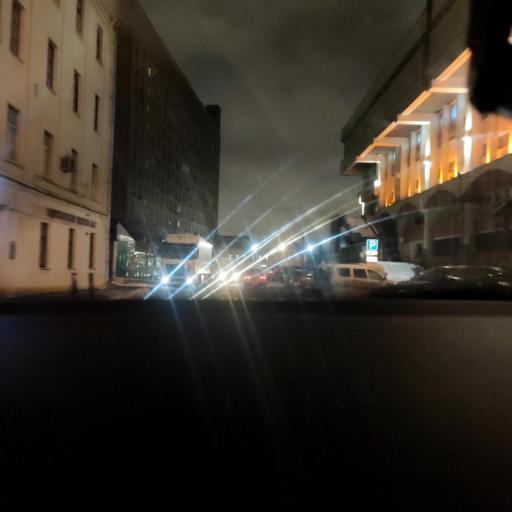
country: RU
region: Moscow
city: Sokol'niki
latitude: 55.7766
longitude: 37.6610
